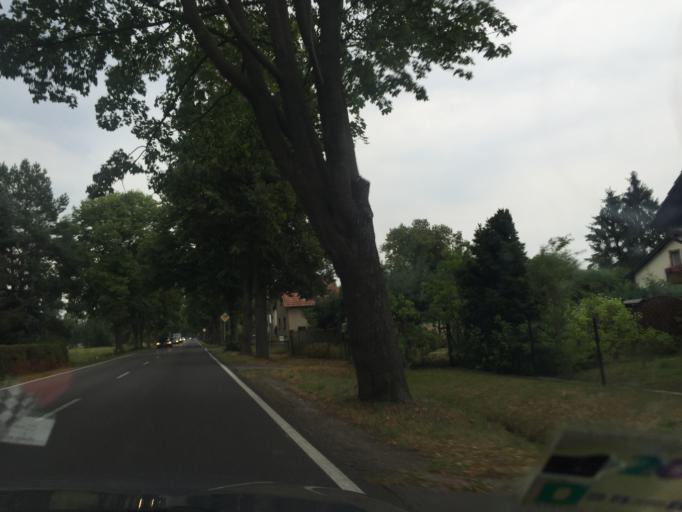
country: DE
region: Brandenburg
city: Wandlitz
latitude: 52.7553
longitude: 13.3886
